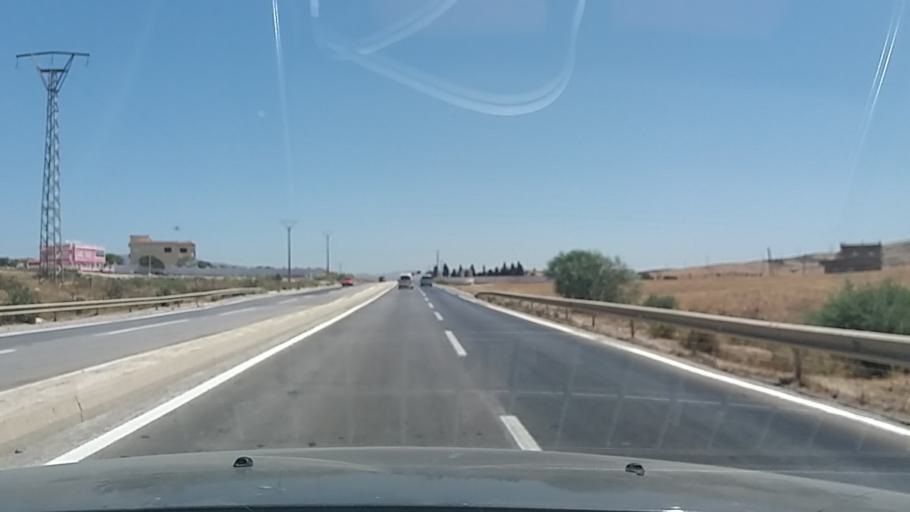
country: MA
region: Tanger-Tetouan
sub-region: Tanger-Assilah
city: Tangier
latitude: 35.6837
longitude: -5.7185
